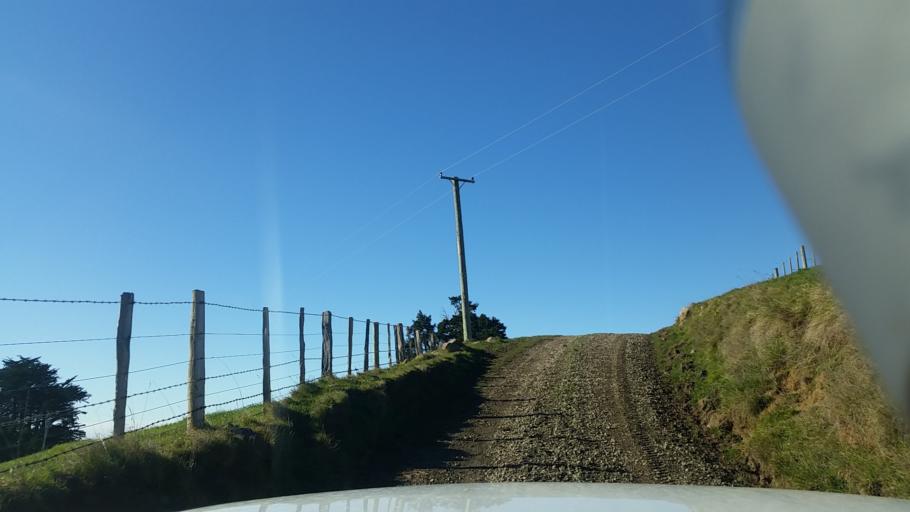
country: NZ
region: Canterbury
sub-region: Christchurch City
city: Christchurch
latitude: -43.6802
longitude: 173.0297
